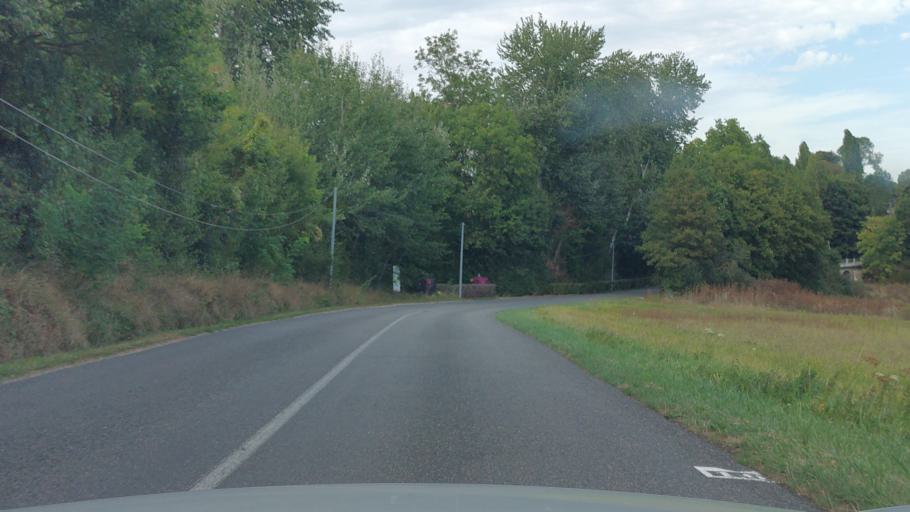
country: FR
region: Ile-de-France
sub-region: Departement de Seine-et-Marne
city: La Chapelle-Gauthier
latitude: 48.5564
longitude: 2.8760
